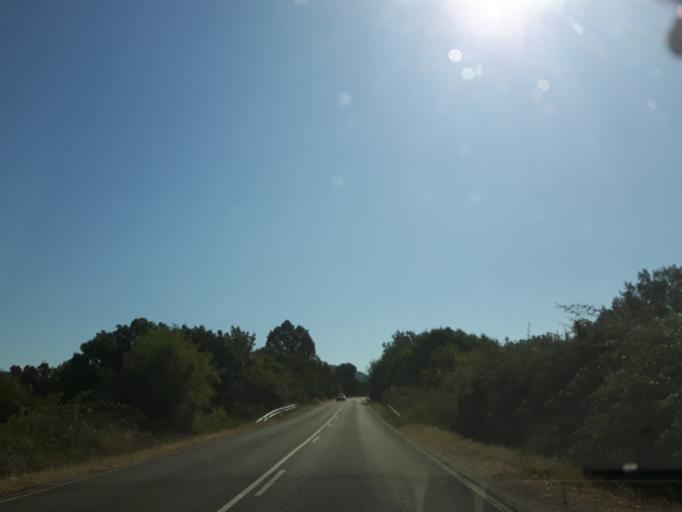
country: ES
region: Castille and Leon
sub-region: Provincia de Salamanca
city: Navalmoral de Bejar
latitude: 40.4092
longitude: -5.8037
